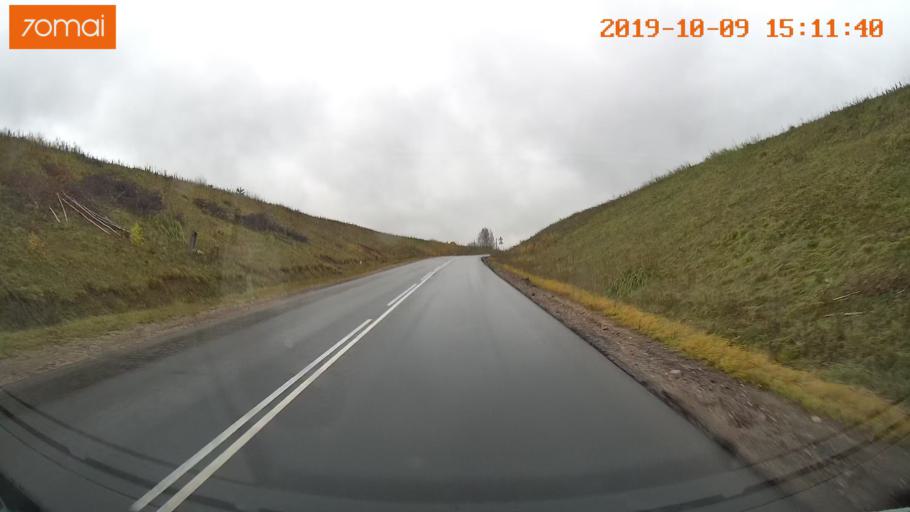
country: RU
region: Kostroma
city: Susanino
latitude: 58.1619
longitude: 41.6287
